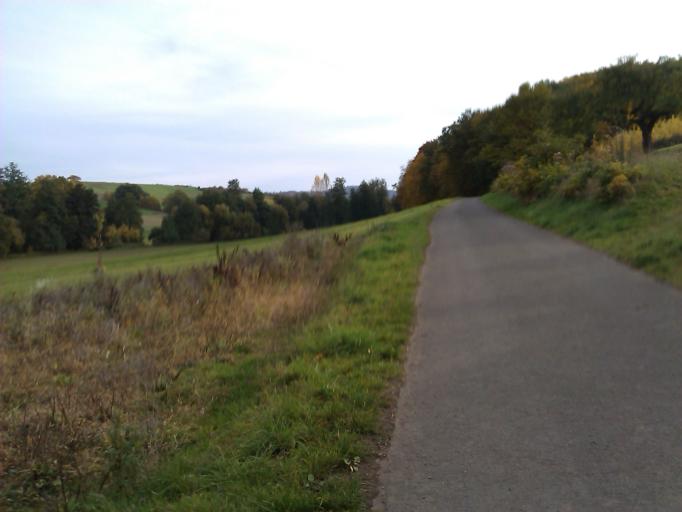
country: DE
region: Rheinland-Pfalz
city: Reipoltskirchen
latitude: 49.6271
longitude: 7.6694
